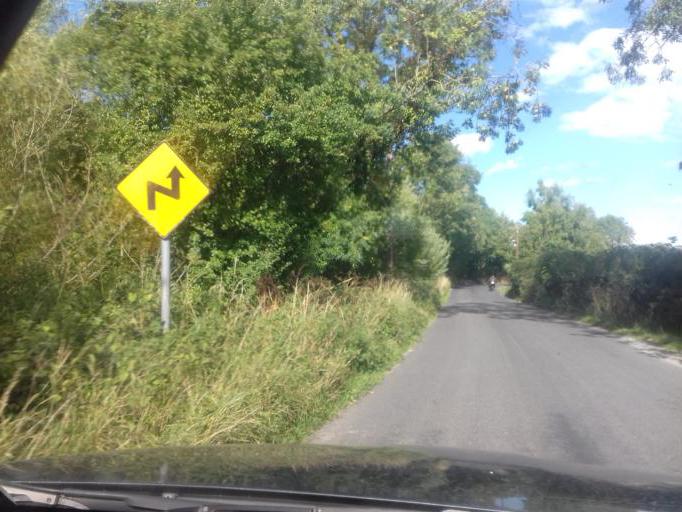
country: IE
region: Leinster
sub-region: Kilkenny
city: Kilkenny
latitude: 52.5393
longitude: -7.2584
